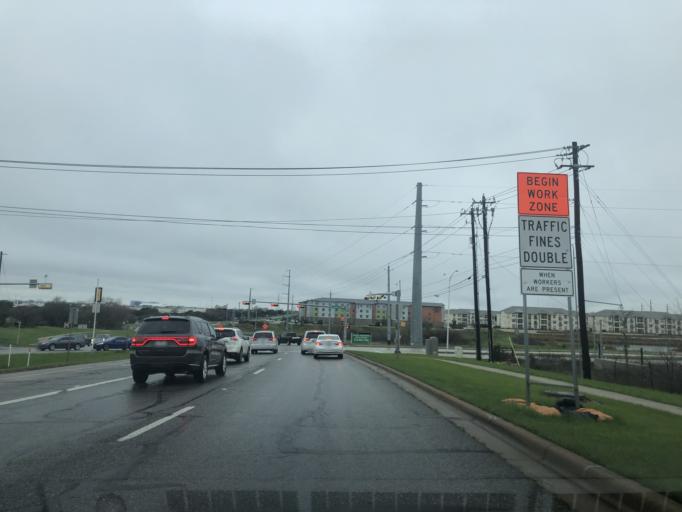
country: US
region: Texas
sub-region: Travis County
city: Wells Branch
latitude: 30.4051
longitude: -97.6631
